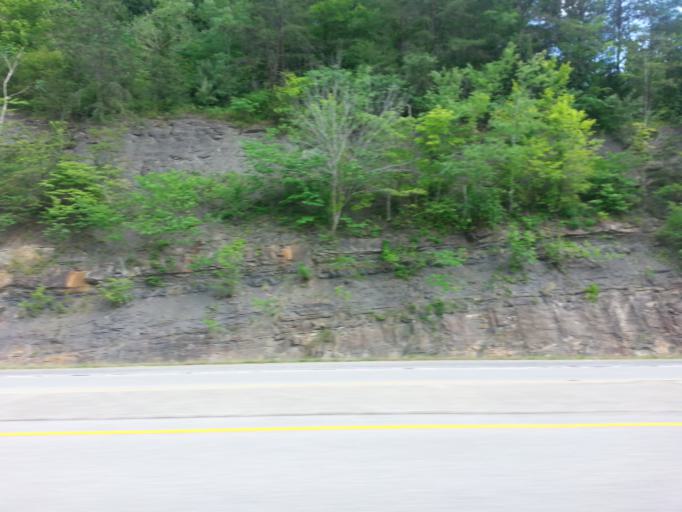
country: US
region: Kentucky
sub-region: Harlan County
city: Harlan
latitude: 36.8716
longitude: -83.3073
